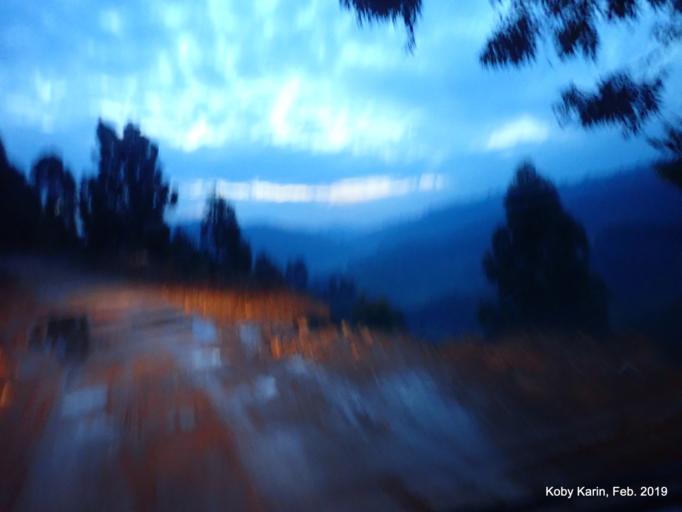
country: UG
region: Western Region
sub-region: Kisoro District
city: Kisoro
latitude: -1.1491
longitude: 29.7462
